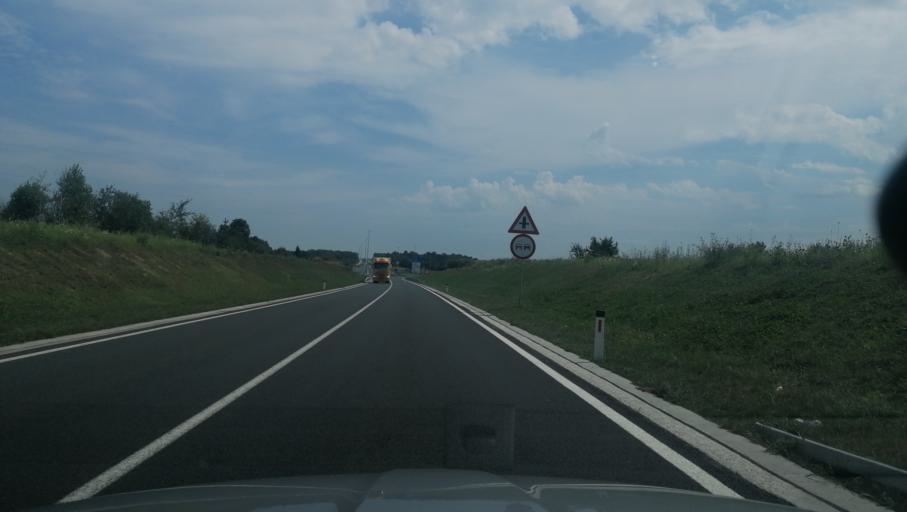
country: BA
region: Brcko
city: Brcko
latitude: 44.8360
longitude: 18.7828
